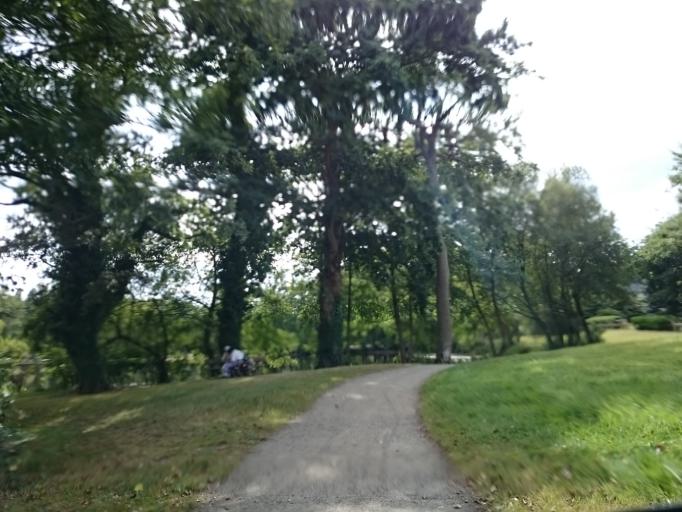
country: FR
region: Brittany
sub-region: Departement d'Ille-et-Vilaine
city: Cesson-Sevigne
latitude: 48.1197
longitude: -1.5930
